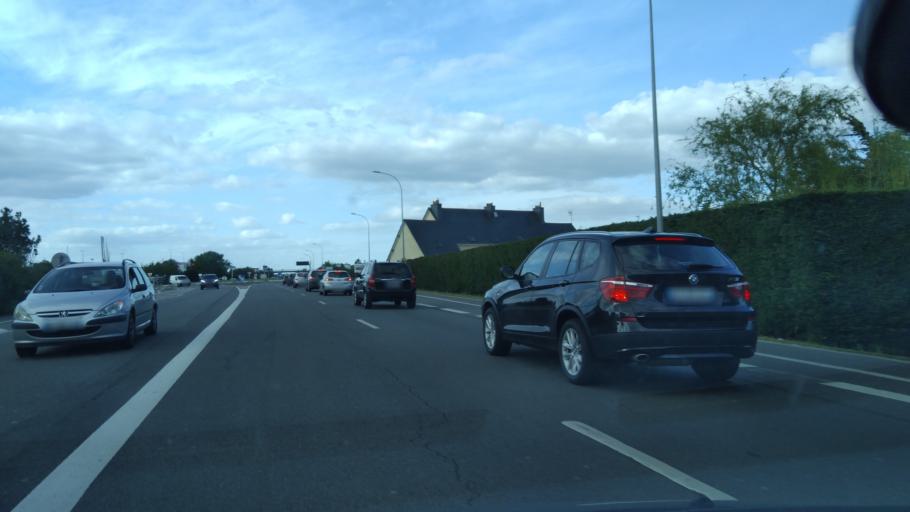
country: FR
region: Pays de la Loire
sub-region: Departement de la Loire-Atlantique
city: Saint-Nazaire
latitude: 47.2976
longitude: -2.2074
